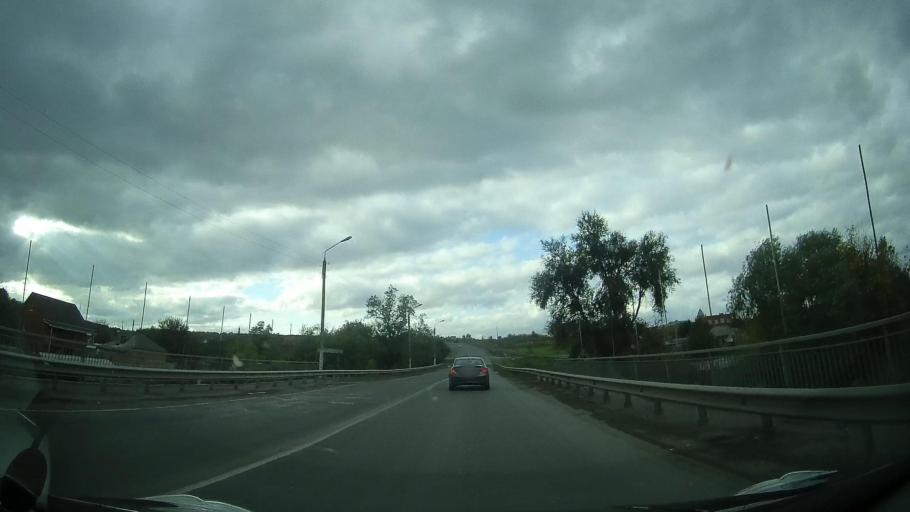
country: RU
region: Rostov
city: Kagal'nitskaya
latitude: 46.8851
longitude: 40.1447
